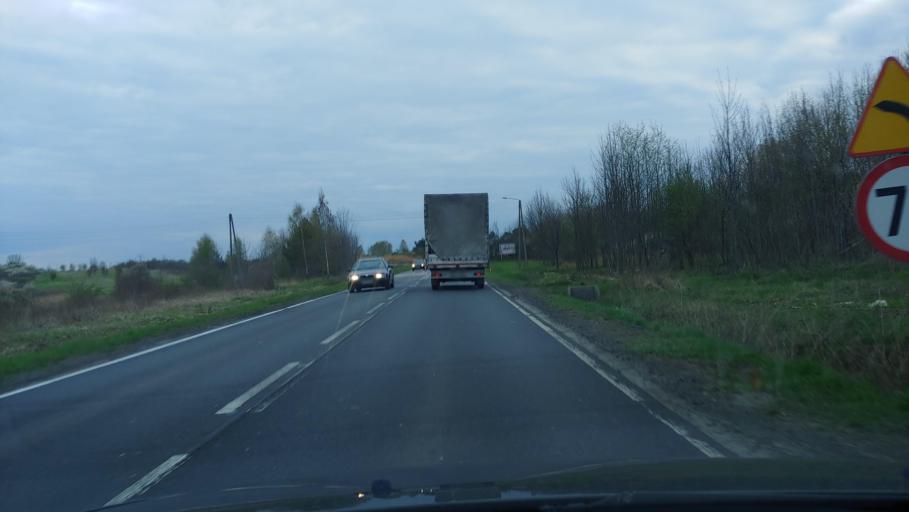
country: PL
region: Lesser Poland Voivodeship
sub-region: Powiat chrzanowski
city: Libiaz
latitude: 50.1609
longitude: 19.3210
